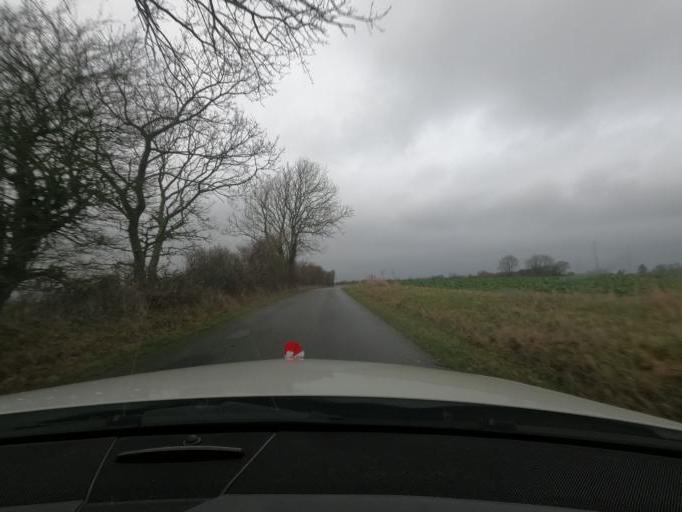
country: DK
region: South Denmark
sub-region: Haderslev Kommune
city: Starup
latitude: 55.1964
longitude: 9.6422
